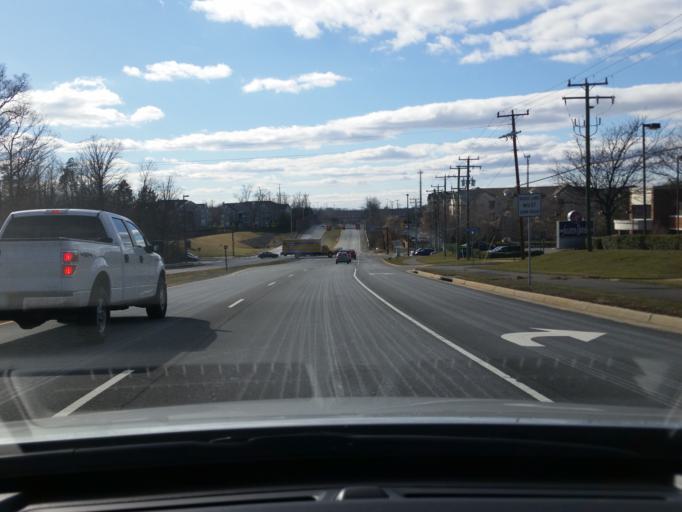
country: US
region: Virginia
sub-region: Fairfax County
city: Reston
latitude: 38.9664
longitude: -77.3582
